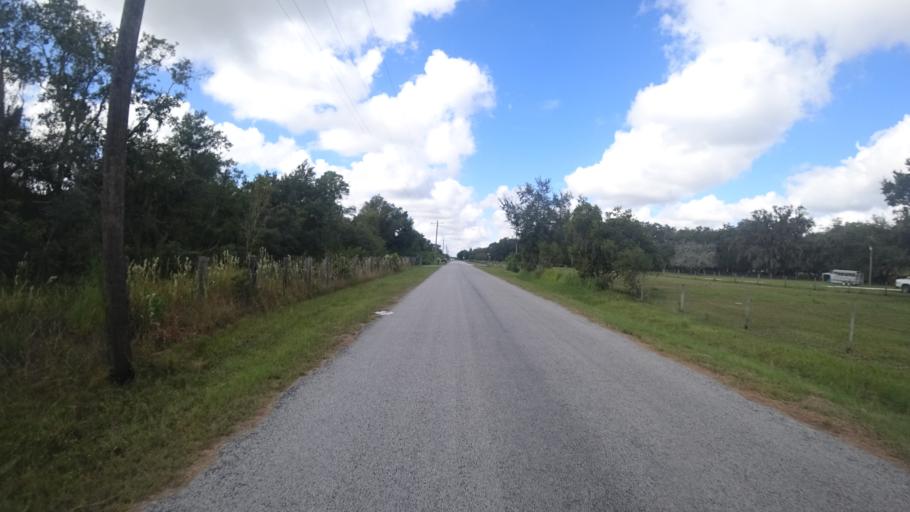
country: US
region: Florida
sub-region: Sarasota County
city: Lake Sarasota
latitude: 27.4011
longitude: -82.2607
